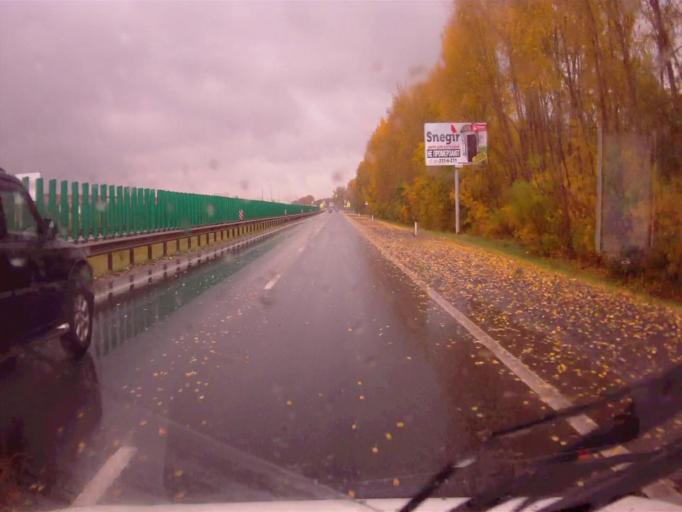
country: RU
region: Chelyabinsk
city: Dolgoderevenskoye
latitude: 55.2798
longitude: 61.3434
